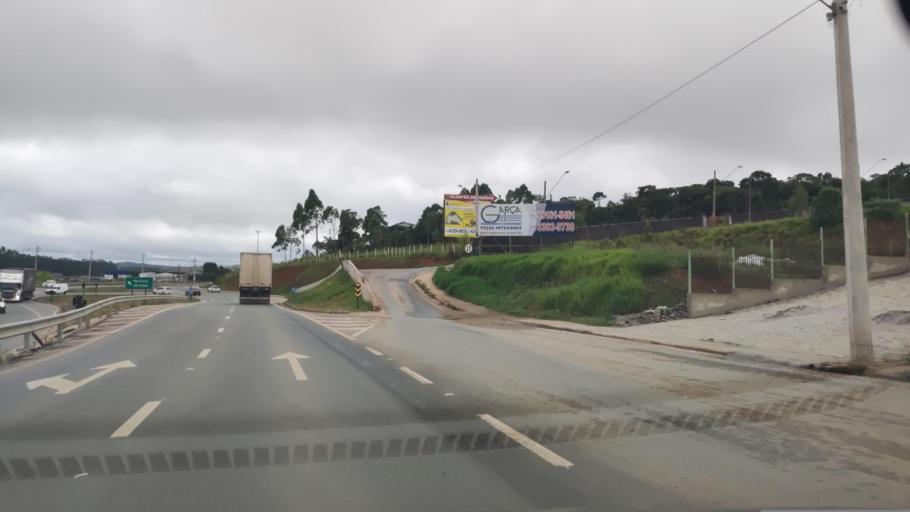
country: BR
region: Sao Paulo
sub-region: Vargem Grande Paulista
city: Vargem Grande Paulista
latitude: -23.6235
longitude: -47.0478
